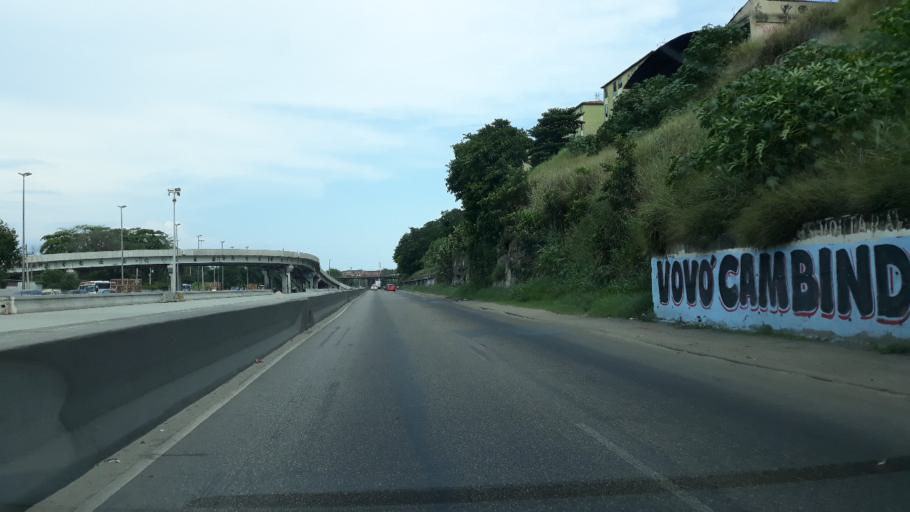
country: BR
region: Rio de Janeiro
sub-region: Duque De Caxias
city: Duque de Caxias
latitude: -22.8150
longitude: -43.2926
